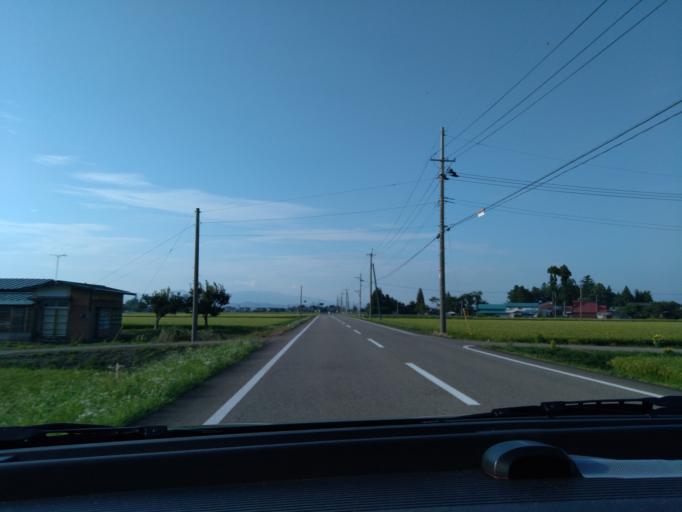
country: JP
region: Akita
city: Kakunodatemachi
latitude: 39.5130
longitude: 140.5588
